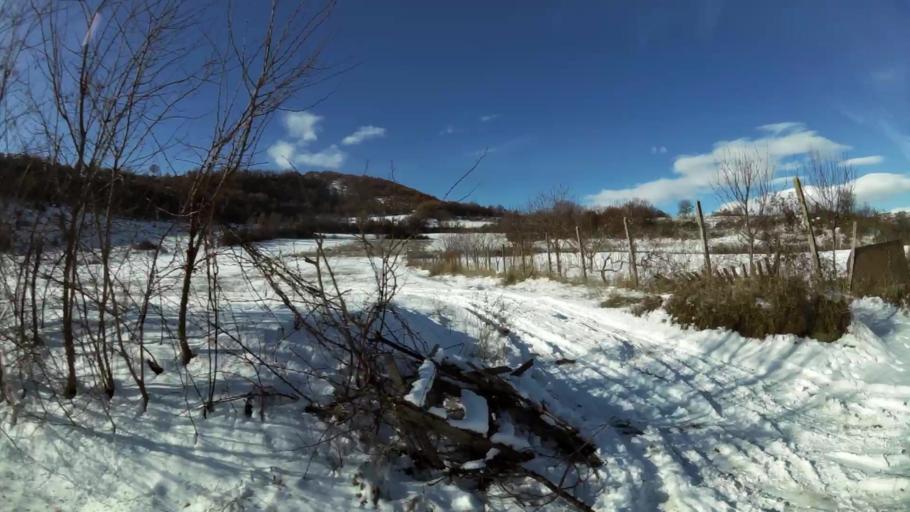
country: MK
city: Ljubin
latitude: 41.9822
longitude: 21.3003
